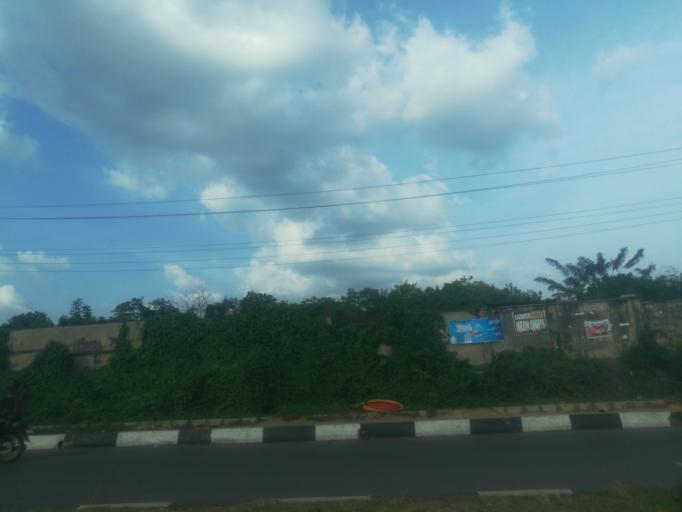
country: NG
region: Ogun
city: Abeokuta
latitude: 7.1323
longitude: 3.3326
